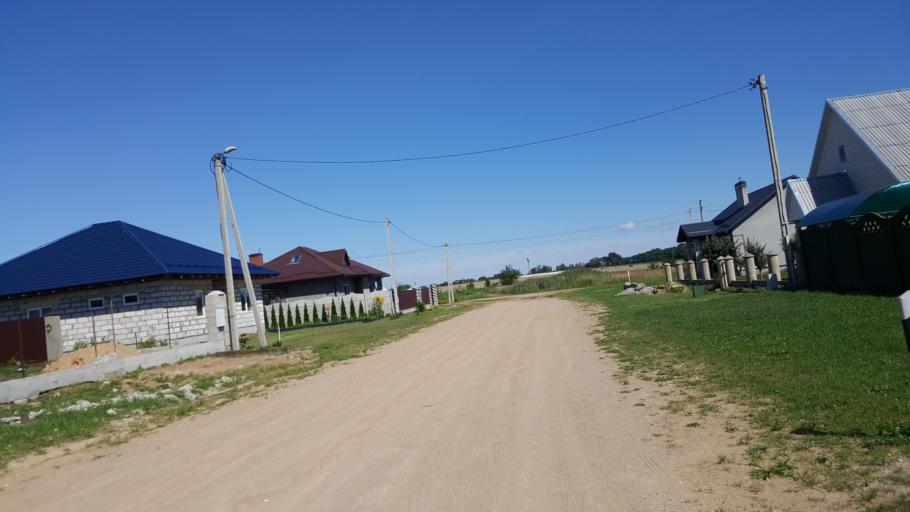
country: BY
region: Brest
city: Charnawchytsy
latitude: 52.2074
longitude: 23.7508
